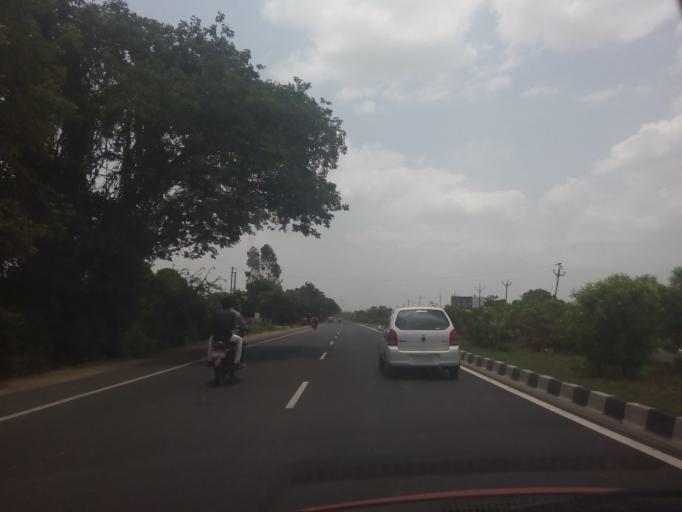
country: IN
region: Gujarat
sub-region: Ahmadabad
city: Sanand
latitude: 22.9856
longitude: 72.4415
